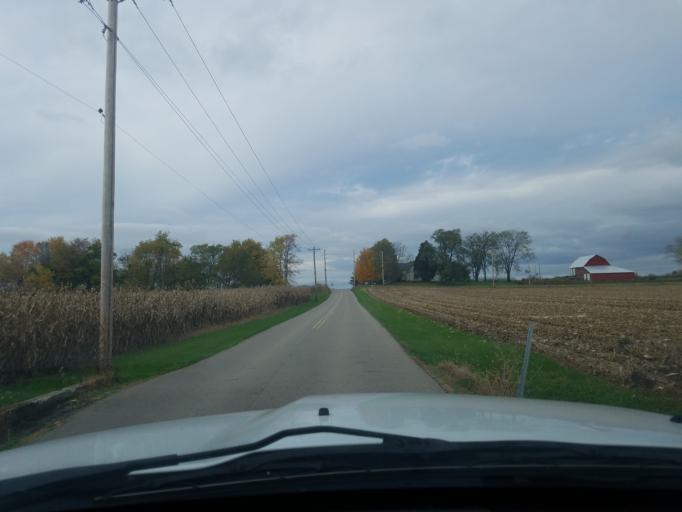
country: US
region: Indiana
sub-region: Shelby County
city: Shelbyville
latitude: 39.5374
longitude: -85.8947
